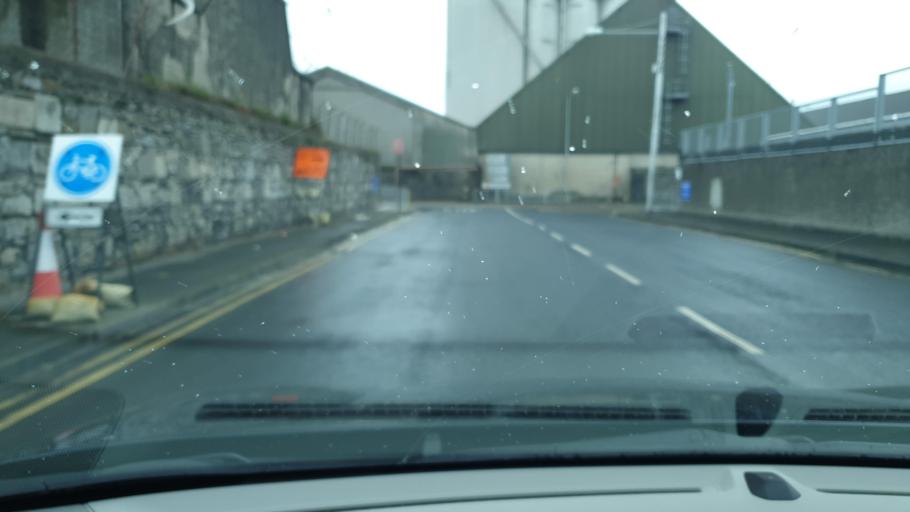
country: IE
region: Leinster
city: Ringsend
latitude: 53.3515
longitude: -6.2194
